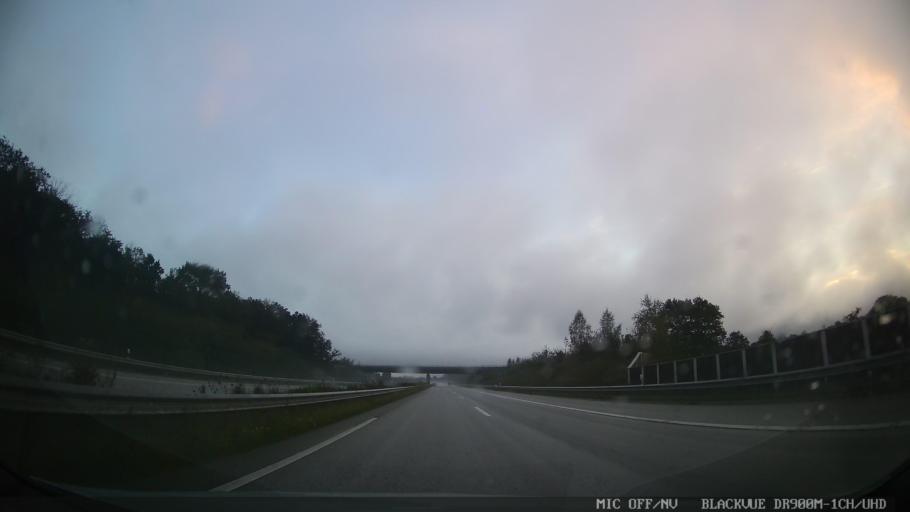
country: DE
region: Schleswig-Holstein
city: Monkhagen
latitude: 53.8881
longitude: 10.5635
